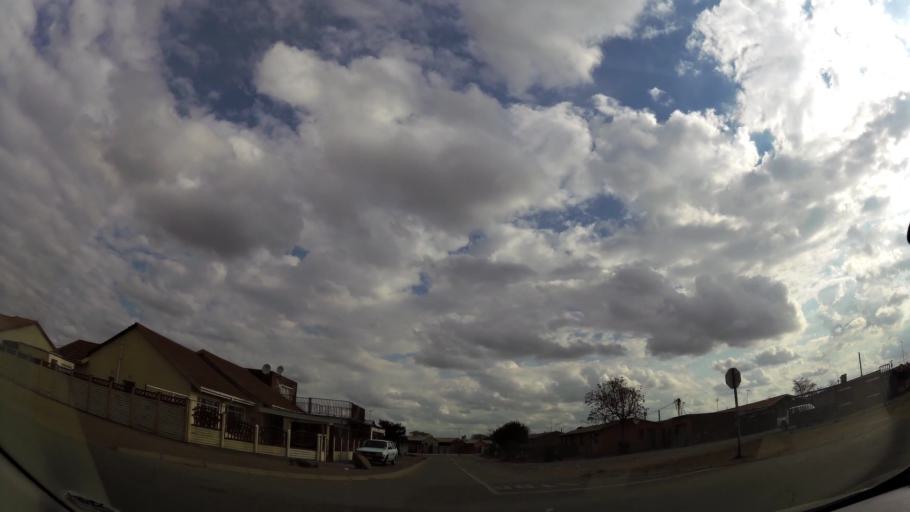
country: ZA
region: Orange Free State
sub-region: Fezile Dabi District Municipality
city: Sasolburg
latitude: -26.8403
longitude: 27.8454
